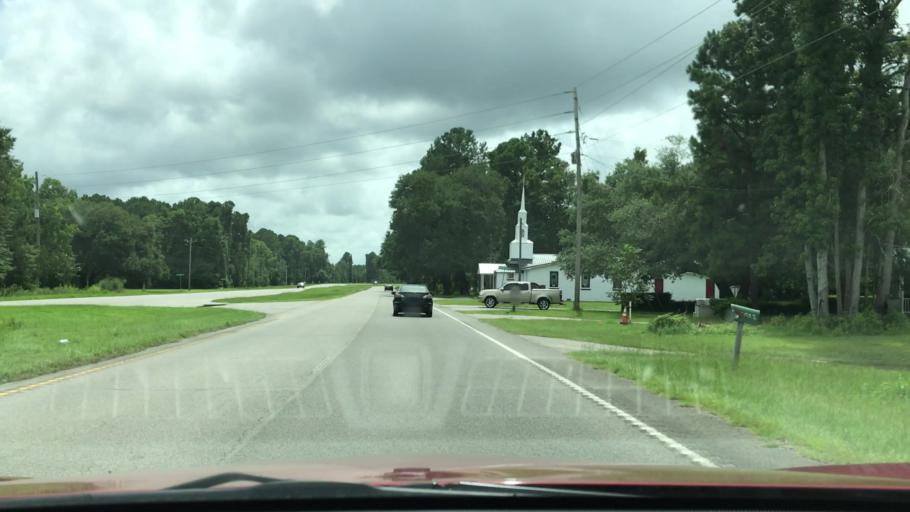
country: US
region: South Carolina
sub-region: Charleston County
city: Awendaw
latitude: 33.0432
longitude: -79.5879
